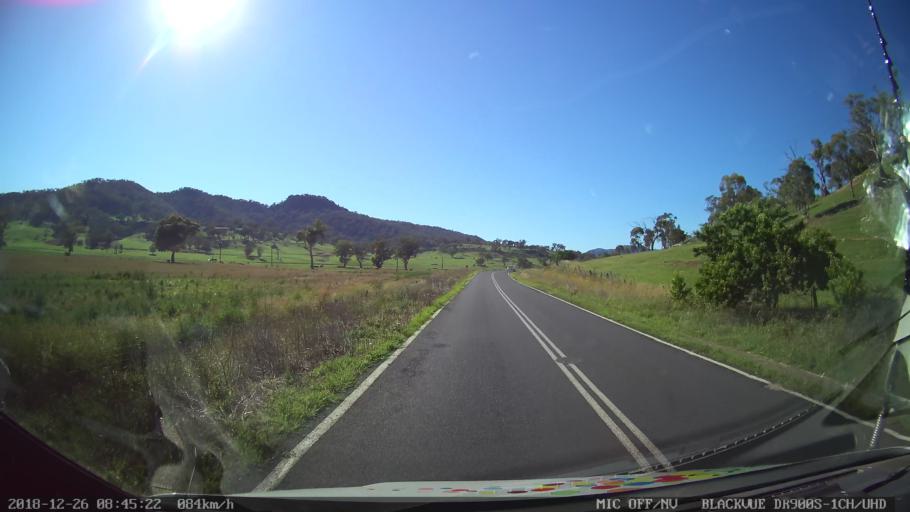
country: AU
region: New South Wales
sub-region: Mid-Western Regional
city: Kandos
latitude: -32.5243
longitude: 150.0863
